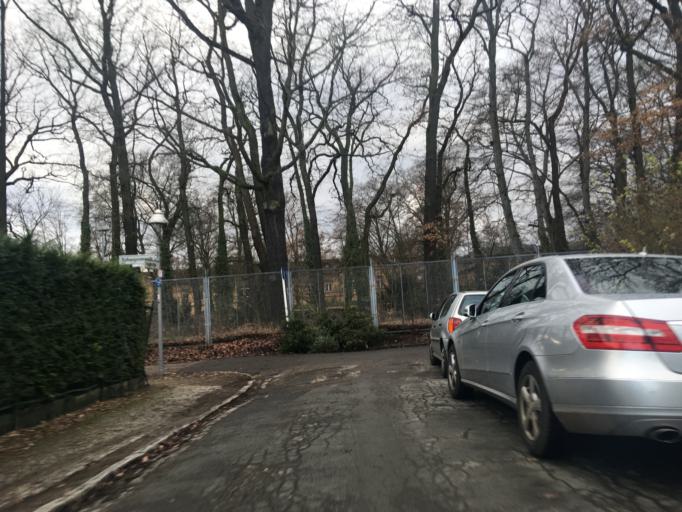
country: DE
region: Berlin
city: Wittenau
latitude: 52.5825
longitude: 13.3325
